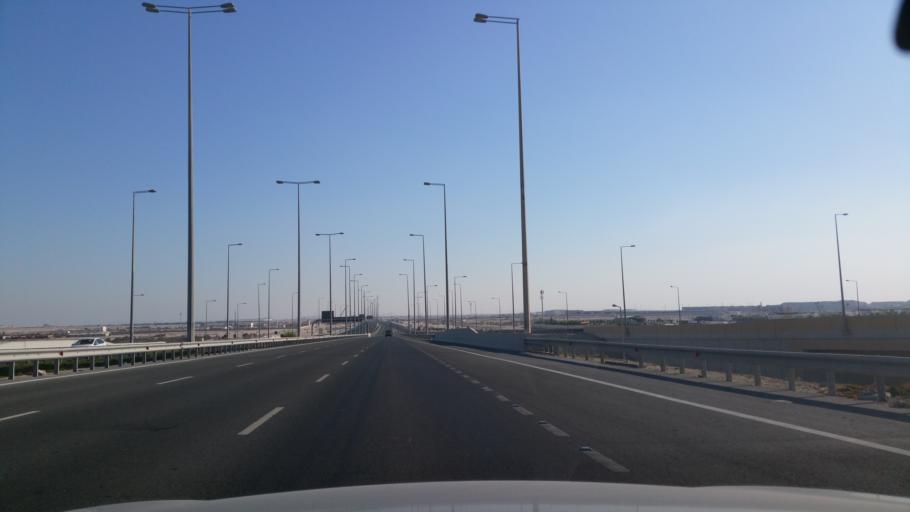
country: QA
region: Al Wakrah
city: Al Wukayr
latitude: 25.1639
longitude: 51.4723
